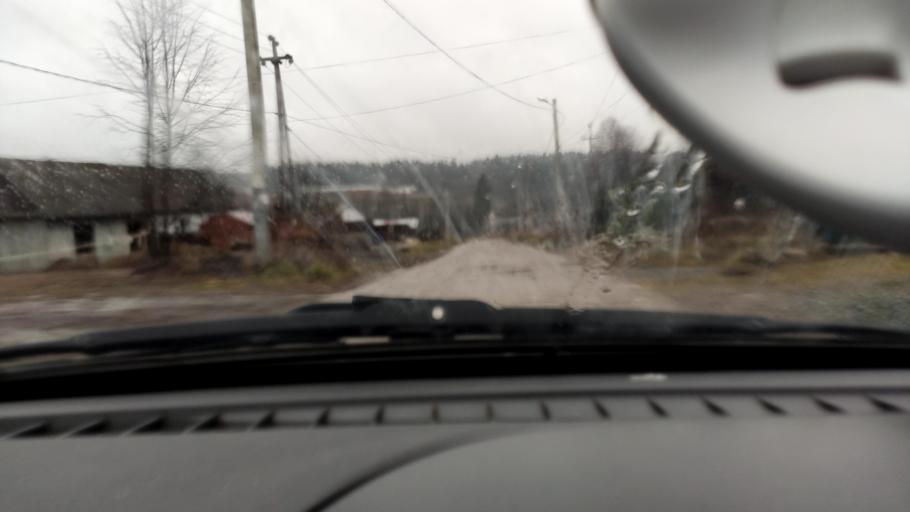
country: RU
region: Perm
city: Perm
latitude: 58.0373
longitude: 56.4086
